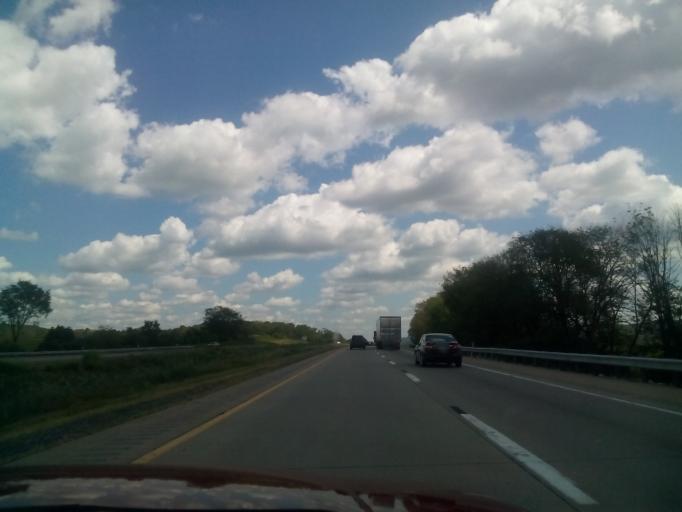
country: US
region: Pennsylvania
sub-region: Northumberland County
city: Riverside
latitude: 40.9870
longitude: -76.7042
